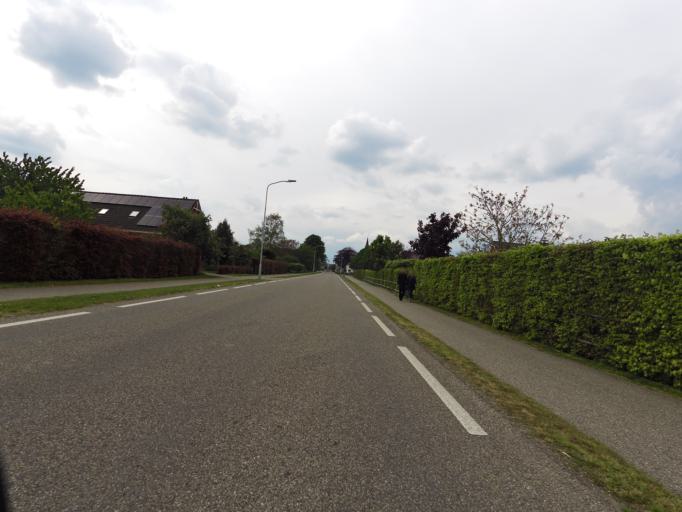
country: NL
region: Gelderland
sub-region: Gemeente Doetinchem
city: Doetinchem
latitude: 51.9348
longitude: 6.2350
